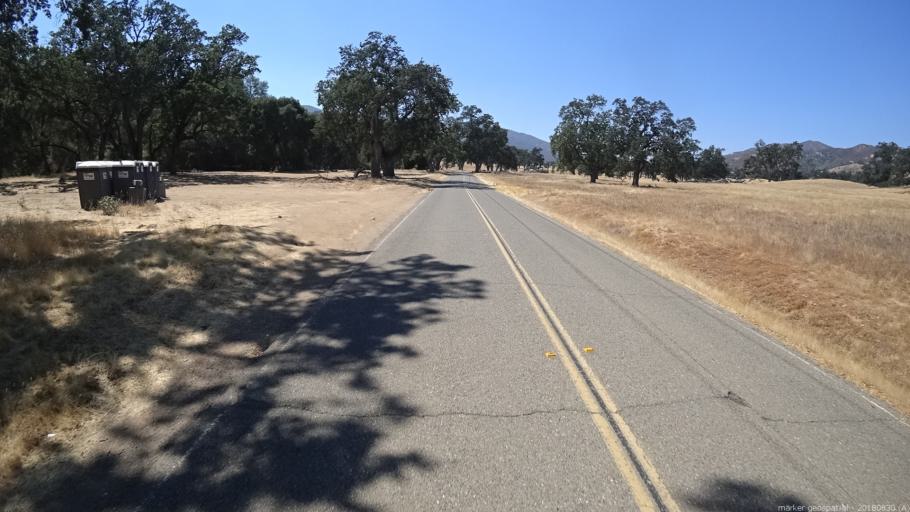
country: US
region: California
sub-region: Monterey County
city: King City
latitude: 35.9732
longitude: -121.3259
